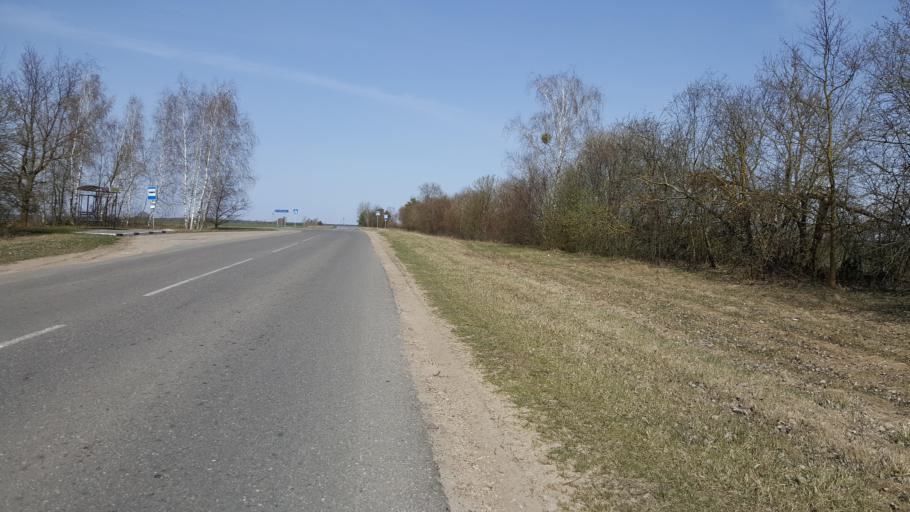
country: BY
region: Brest
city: Kamyanyets
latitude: 52.4734
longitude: 23.7077
